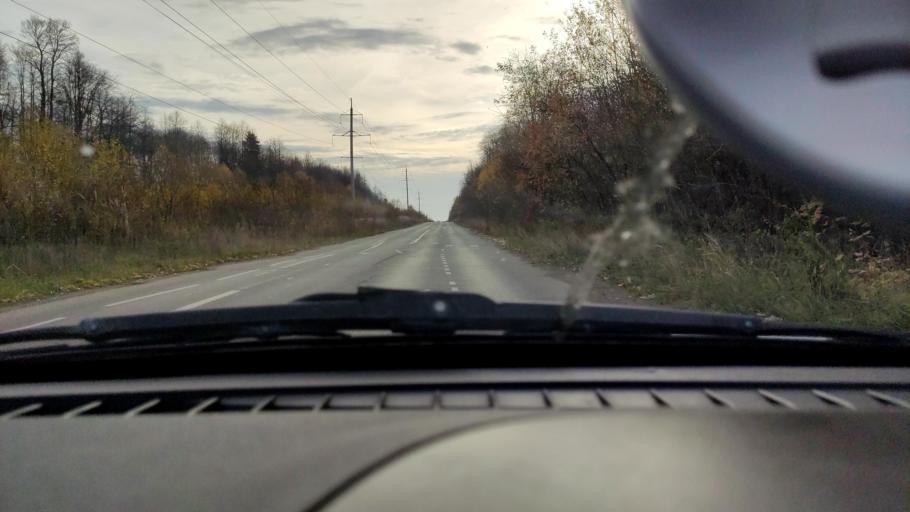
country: RU
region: Perm
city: Perm
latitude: 58.0932
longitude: 56.4067
